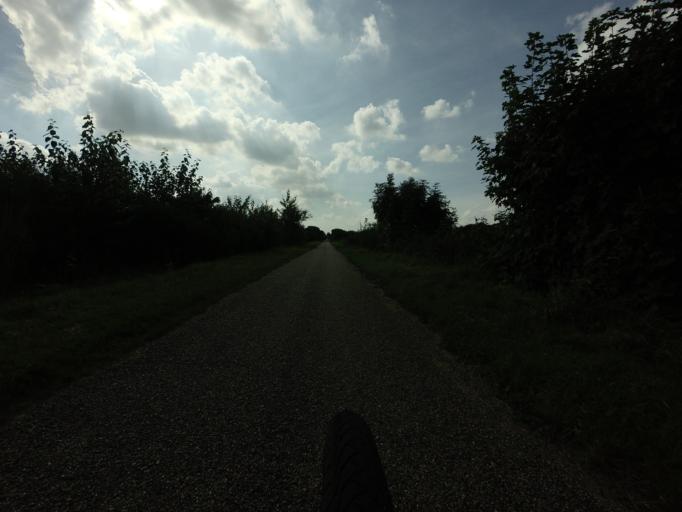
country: DK
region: Central Jutland
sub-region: Herning Kommune
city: Sunds
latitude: 56.2319
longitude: 9.0822
